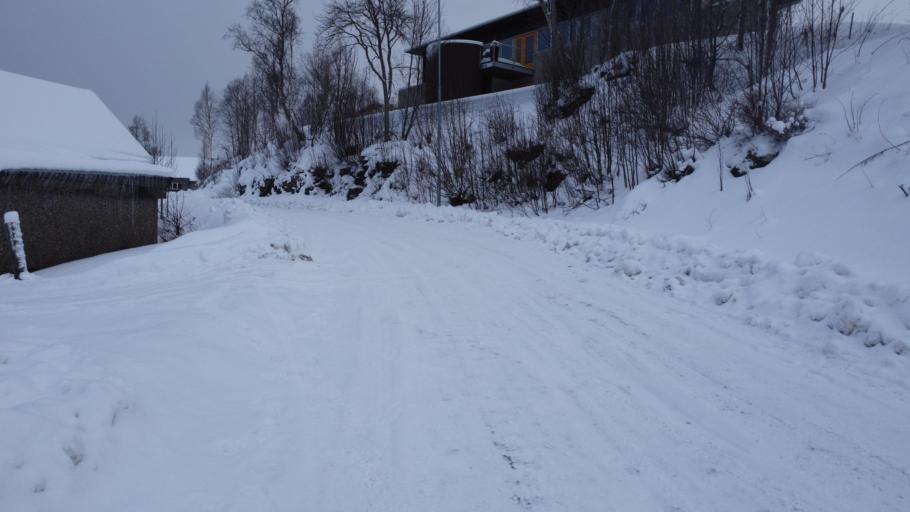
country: NO
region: Nordland
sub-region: Rana
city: Mo i Rana
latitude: 66.3143
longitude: 14.1389
